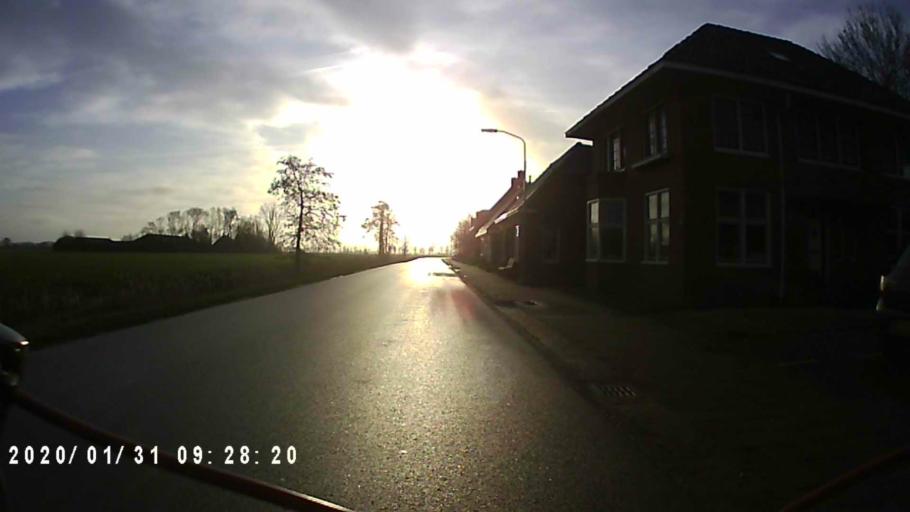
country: NL
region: Groningen
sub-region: Gemeente Zuidhorn
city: Oldehove
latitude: 53.3077
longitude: 6.4436
